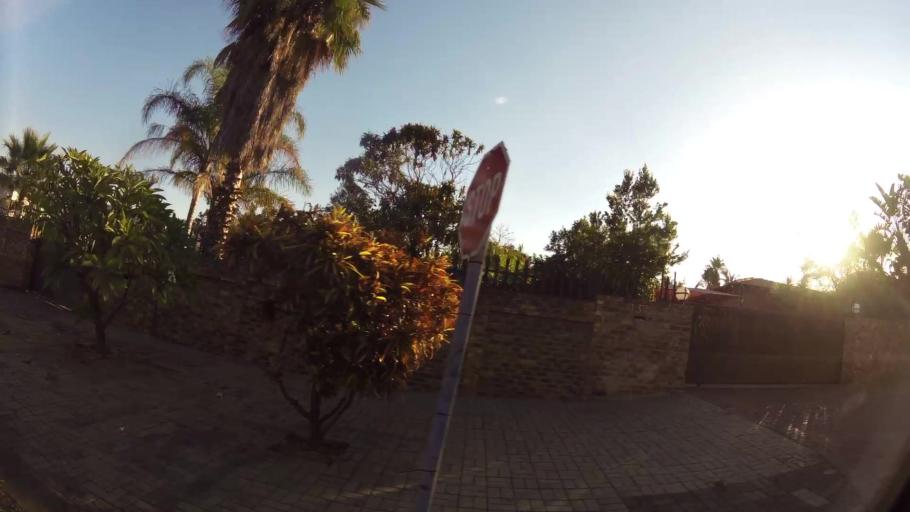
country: ZA
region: North-West
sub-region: Bojanala Platinum District Municipality
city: Rustenburg
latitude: -25.6822
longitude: 27.2034
